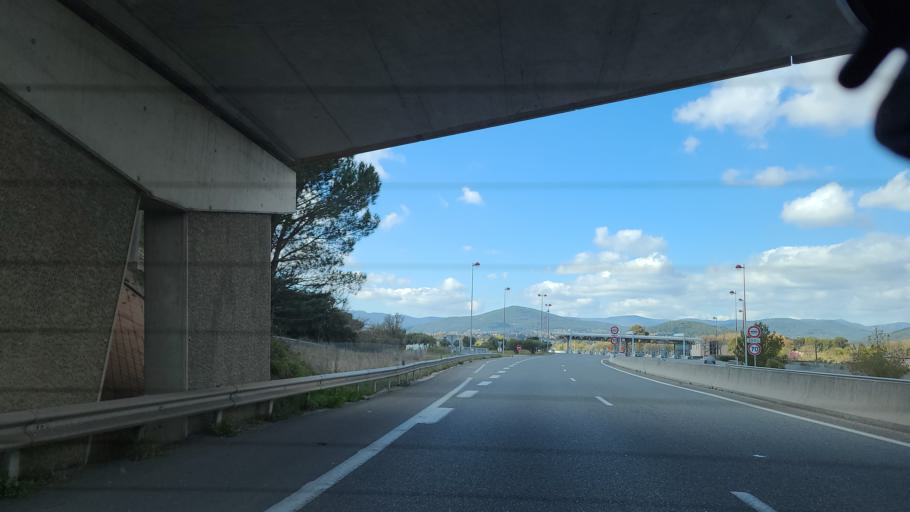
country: FR
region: Provence-Alpes-Cote d'Azur
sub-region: Departement du Var
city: Puget-Ville
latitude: 43.2588
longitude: 6.1257
